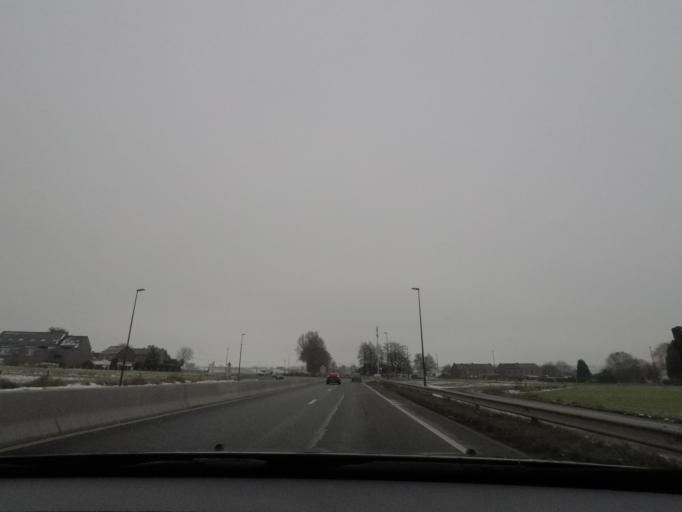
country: BE
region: Wallonia
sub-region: Province de Namur
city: Sombreffe
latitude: 50.4707
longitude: 4.6230
